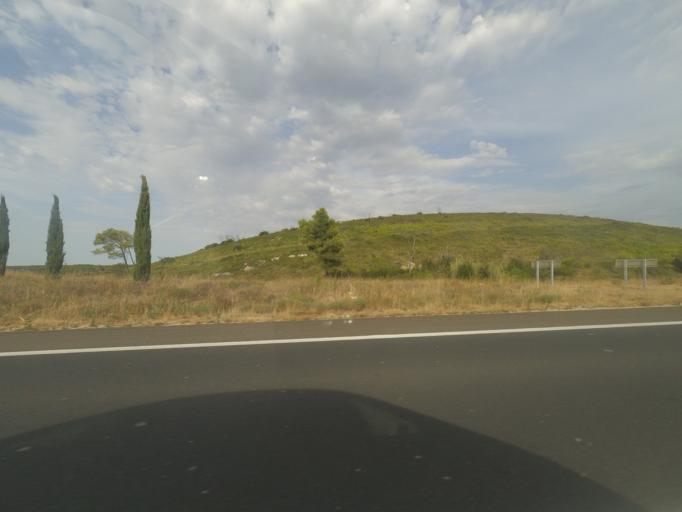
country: FR
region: Languedoc-Roussillon
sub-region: Departement de l'Herault
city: Assas
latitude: 43.7189
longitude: 3.9100
